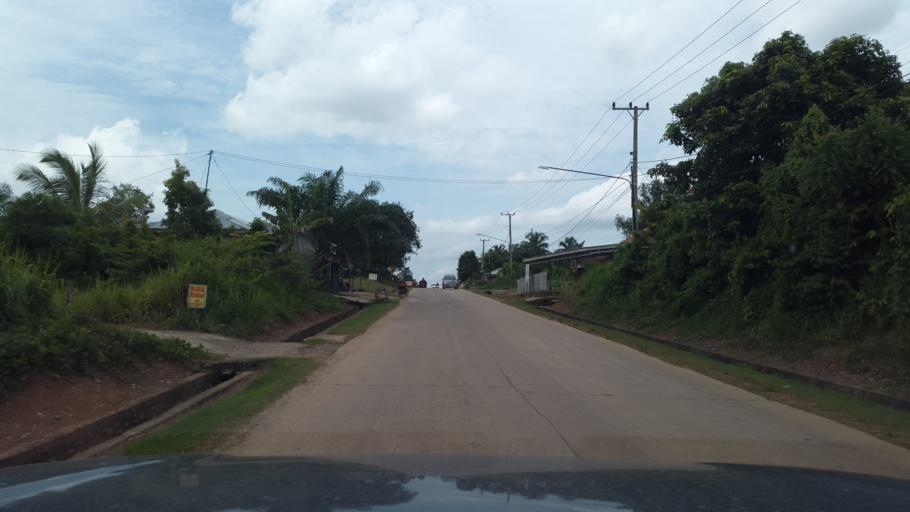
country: ID
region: South Sumatra
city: Gunungmegang Dalam
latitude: -3.3025
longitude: 103.8607
